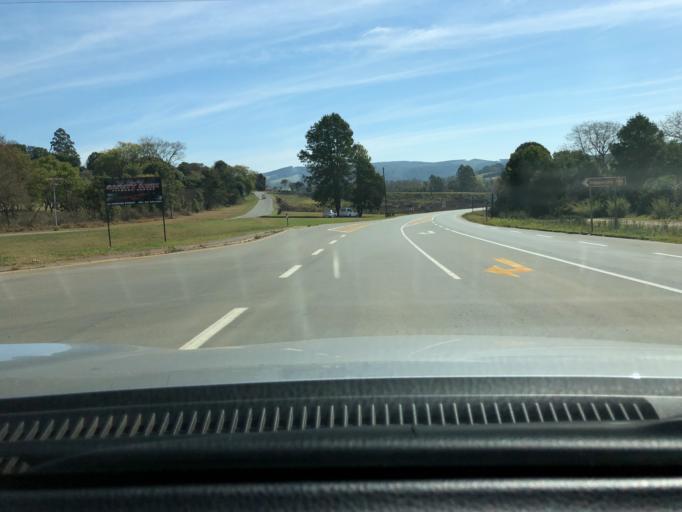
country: ZA
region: KwaZulu-Natal
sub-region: uMgungundlovu District Municipality
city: Richmond
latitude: -29.8779
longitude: 30.2837
